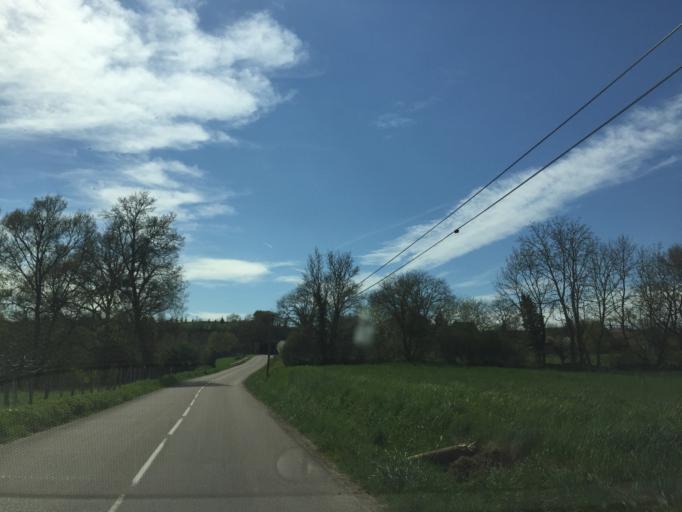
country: FR
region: Rhone-Alpes
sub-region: Departement de l'Isere
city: Trept
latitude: 45.7186
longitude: 5.3245
